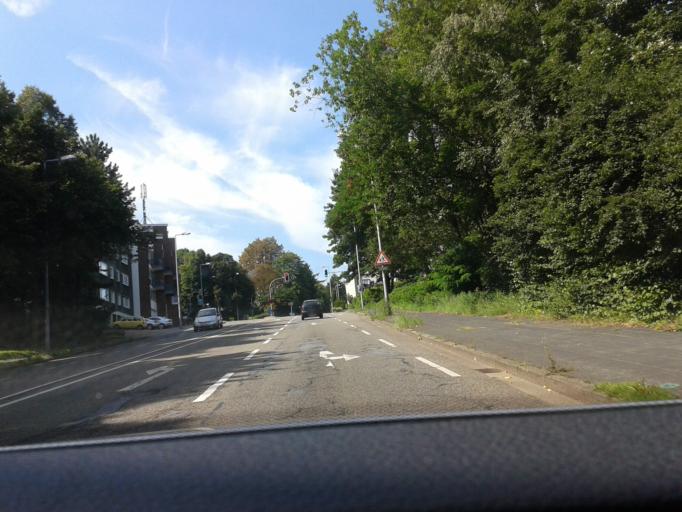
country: DE
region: North Rhine-Westphalia
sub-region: Regierungsbezirk Dusseldorf
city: Muelheim (Ruhr)
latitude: 51.4090
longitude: 6.8661
